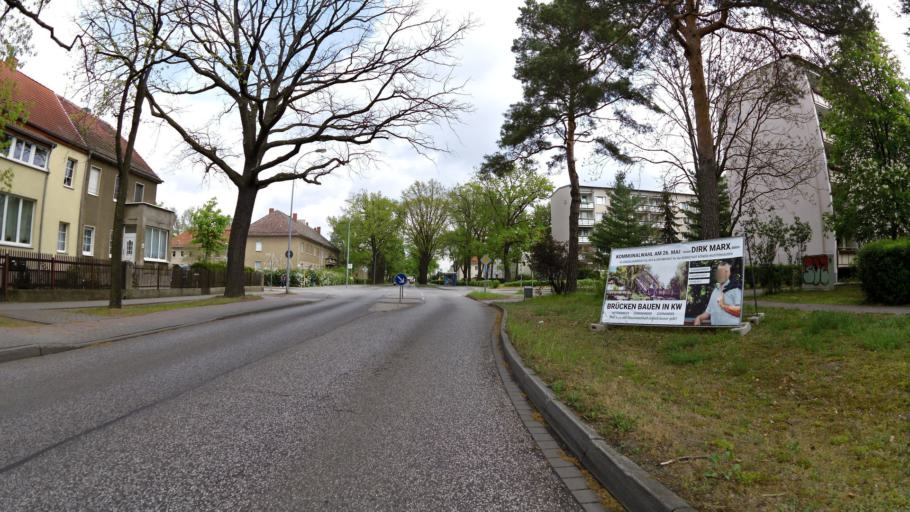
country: DE
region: Brandenburg
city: Konigs Wusterhausen
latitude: 52.2920
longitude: 13.6197
